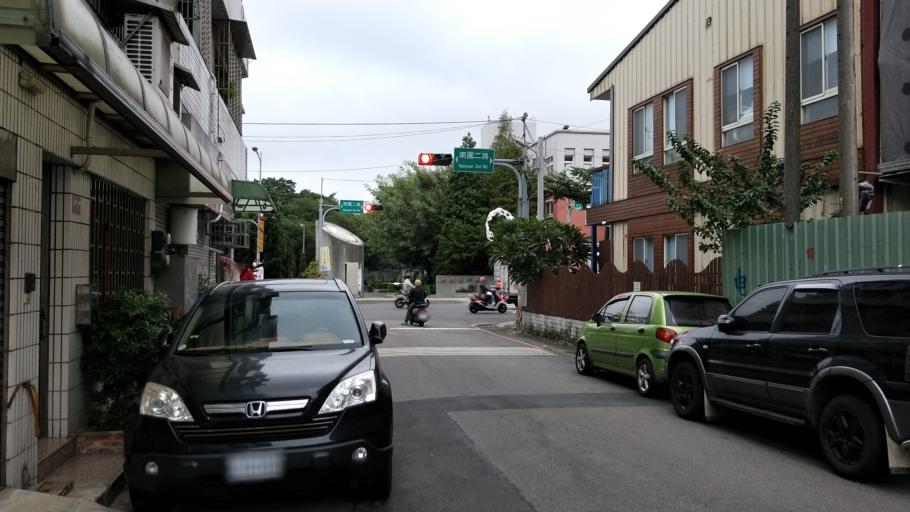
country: TW
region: Taiwan
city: Taoyuan City
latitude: 24.9713
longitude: 121.2331
